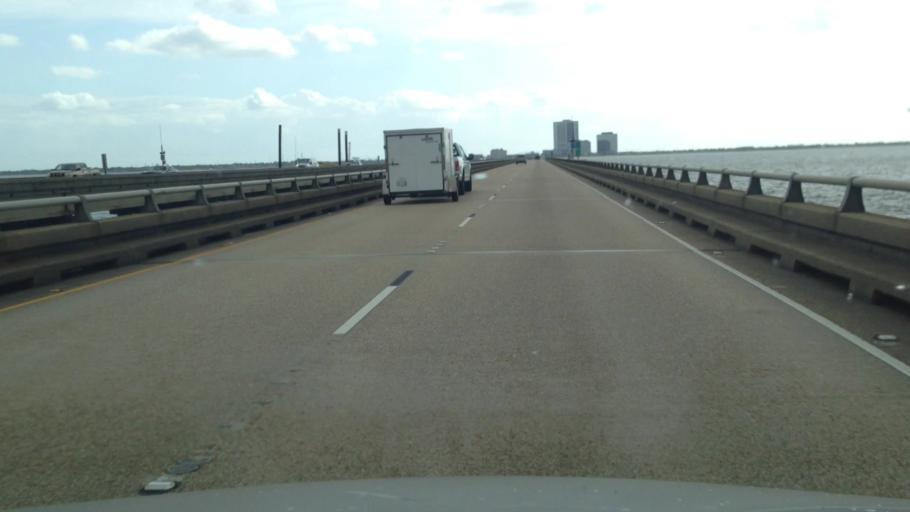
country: US
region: Louisiana
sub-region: Jefferson Parish
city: Metairie
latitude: 30.0469
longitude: -90.1497
